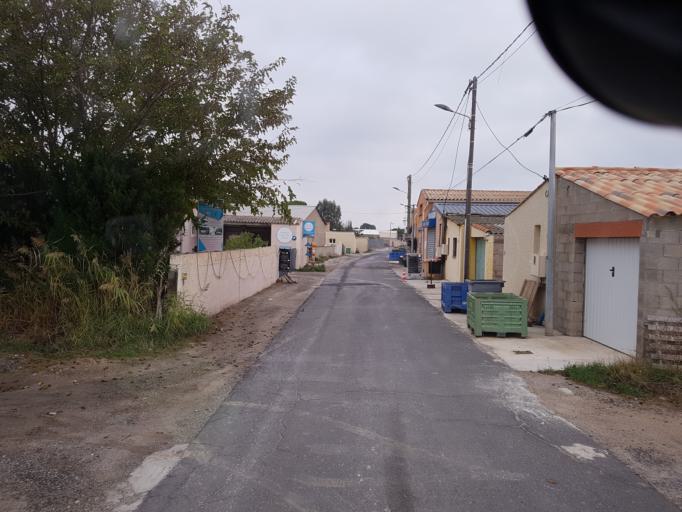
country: FR
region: Languedoc-Roussillon
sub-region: Departement de l'Herault
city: Marseillan
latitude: 43.3635
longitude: 3.5368
